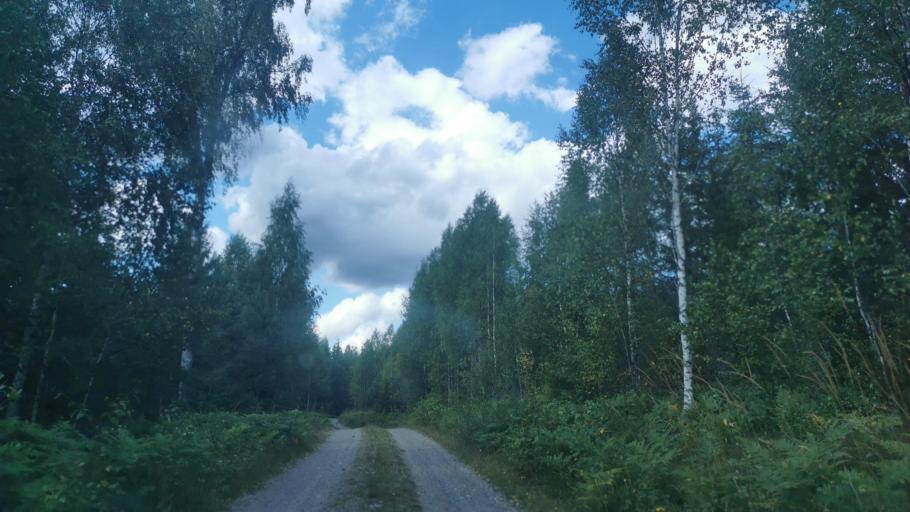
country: SE
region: OEstergoetland
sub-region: Finspangs Kommun
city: Finspang
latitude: 58.7994
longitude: 15.7857
